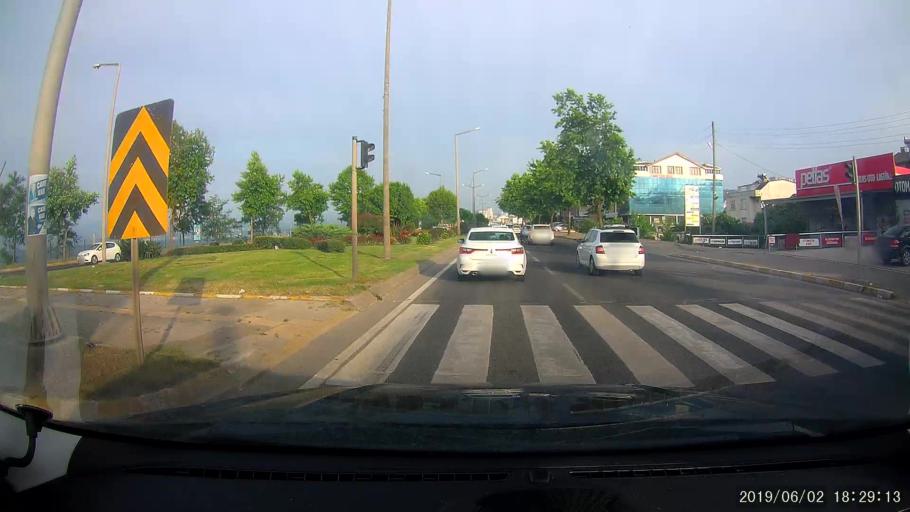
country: TR
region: Ordu
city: Fatsa
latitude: 41.0395
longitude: 37.4897
